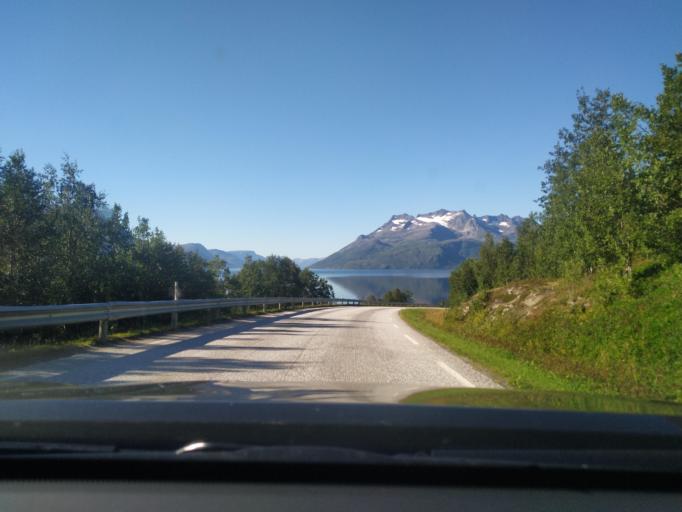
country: NO
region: Troms
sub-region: Dyroy
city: Brostadbotn
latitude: 68.9237
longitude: 17.6372
